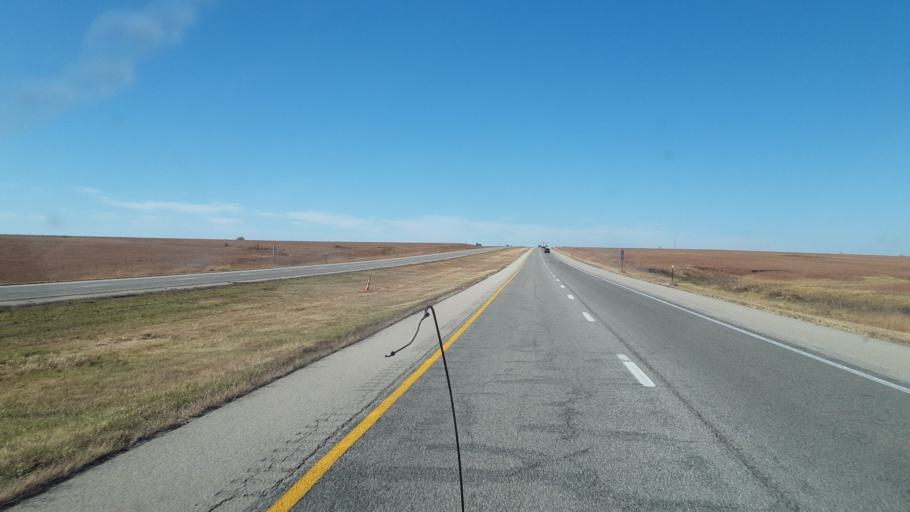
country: US
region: Kansas
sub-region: Osage County
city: Osage City
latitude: 38.4265
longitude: -95.7904
